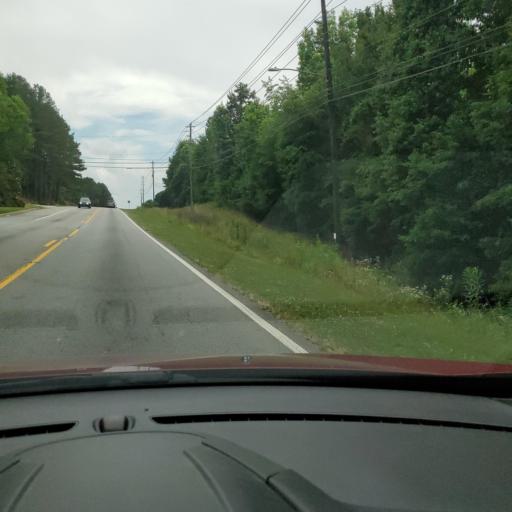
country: US
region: Georgia
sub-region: Henry County
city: Stockbridge
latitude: 33.5187
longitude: -84.2302
